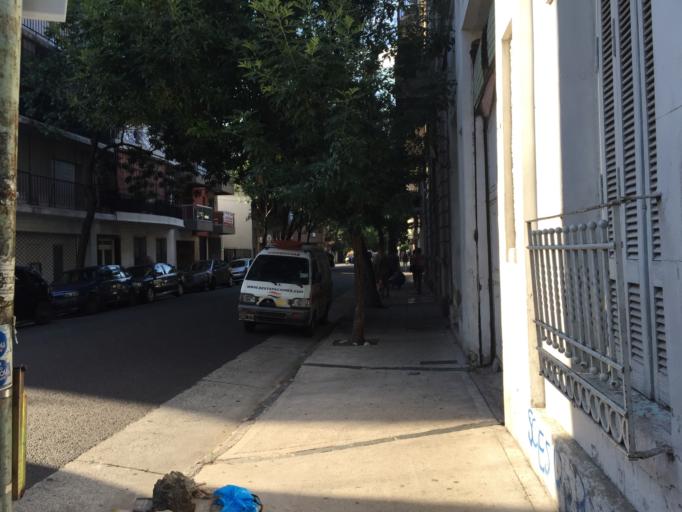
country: AR
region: Buenos Aires F.D.
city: Buenos Aires
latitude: -34.6226
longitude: -58.3980
